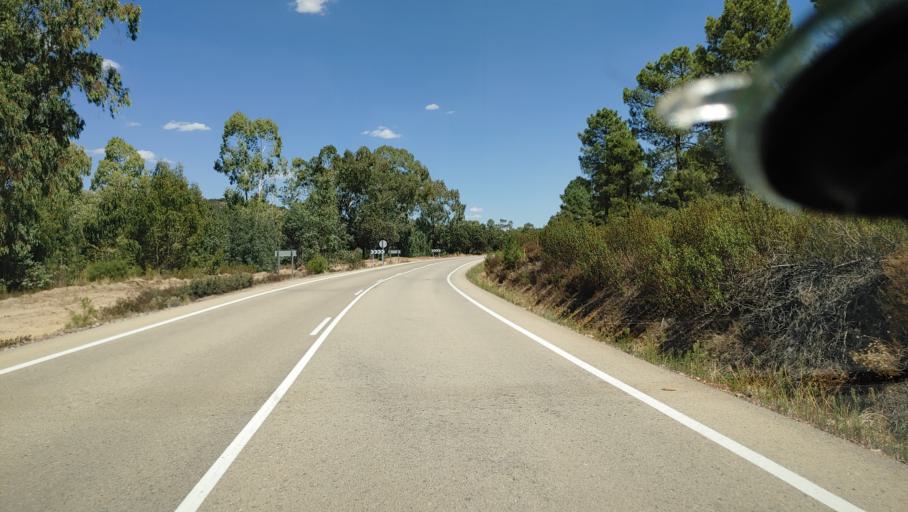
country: ES
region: Castille-La Mancha
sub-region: Provincia de Ciudad Real
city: Saceruela
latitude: 38.9910
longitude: -4.5390
